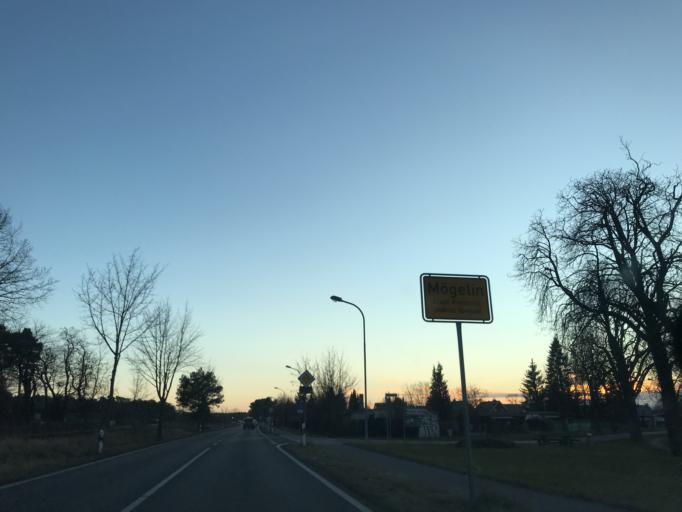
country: DE
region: Brandenburg
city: Premnitz
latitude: 52.5653
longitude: 12.3314
